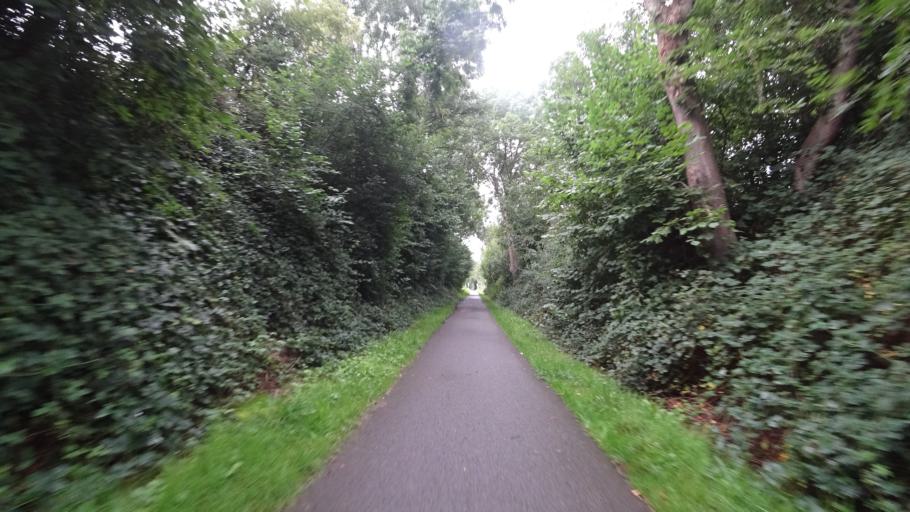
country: BE
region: Wallonia
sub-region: Province de Namur
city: Namur
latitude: 50.5033
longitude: 4.8682
